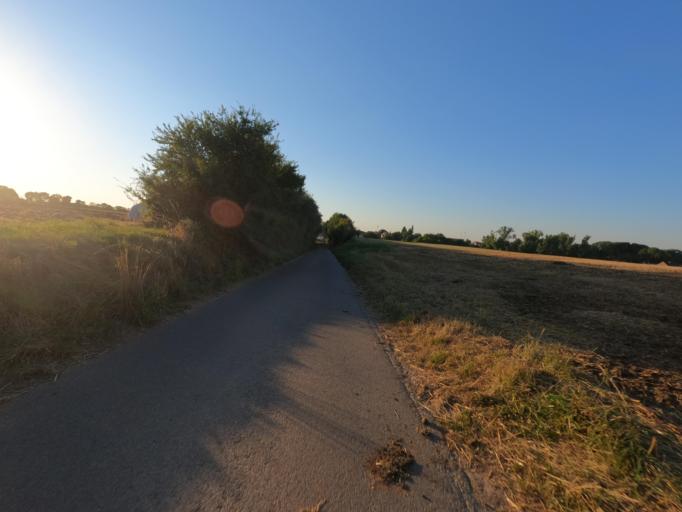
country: DE
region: North Rhine-Westphalia
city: Julich
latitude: 50.9756
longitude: 6.3553
